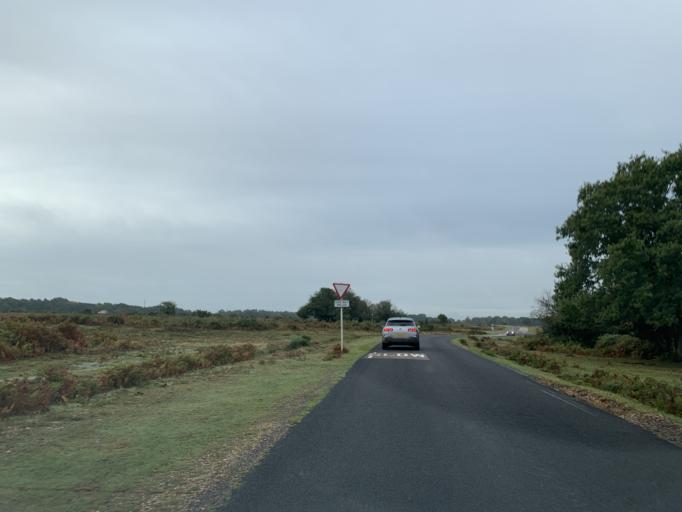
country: GB
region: England
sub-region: Wiltshire
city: Whiteparish
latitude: 50.9403
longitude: -1.6517
